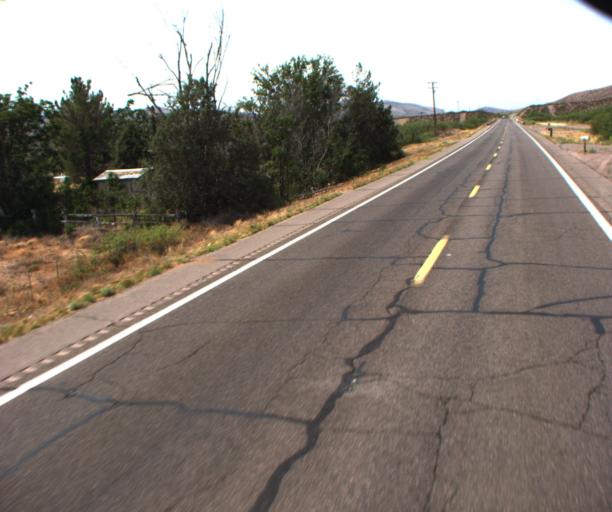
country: US
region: Arizona
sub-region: Greenlee County
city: Clifton
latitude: 32.8231
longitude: -109.1736
